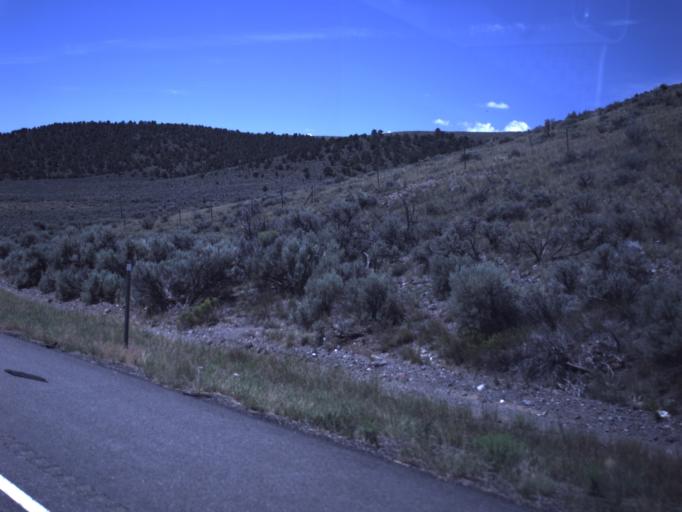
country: US
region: Utah
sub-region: Garfield County
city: Panguitch
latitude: 37.8162
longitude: -112.4038
